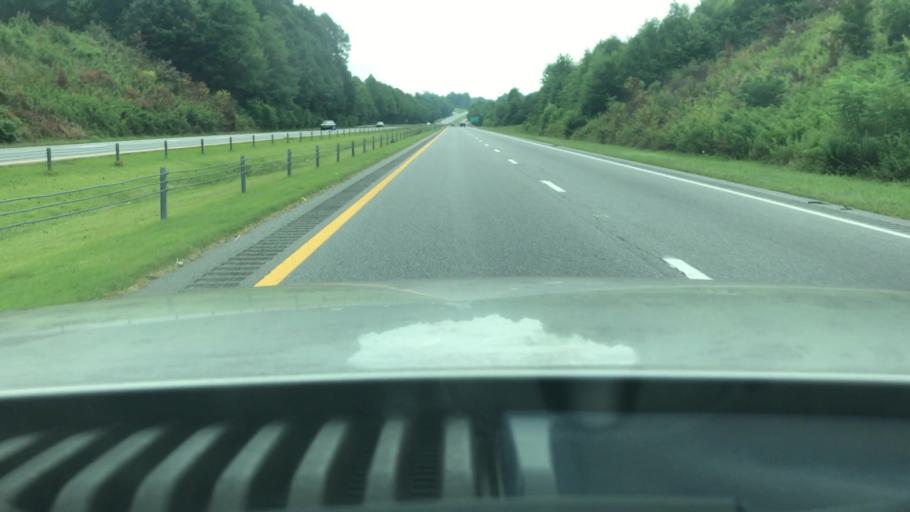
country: US
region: North Carolina
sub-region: Wilkes County
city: North Wilkesboro
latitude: 36.1482
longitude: -81.0354
